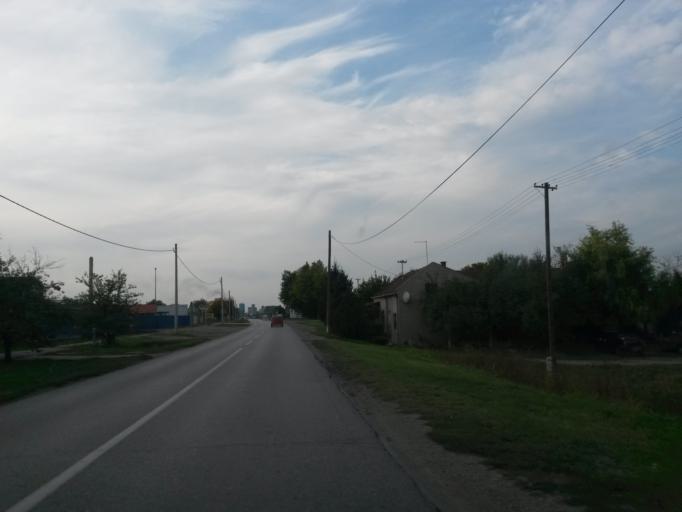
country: HR
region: Osjecko-Baranjska
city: Tenja
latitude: 45.5412
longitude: 18.7598
